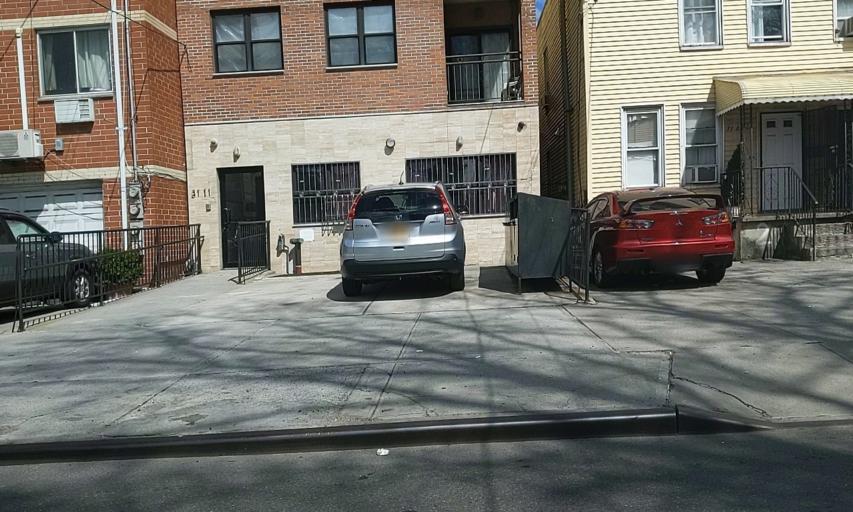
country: US
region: New York
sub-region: Queens County
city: Jamaica
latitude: 40.7689
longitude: -73.8324
